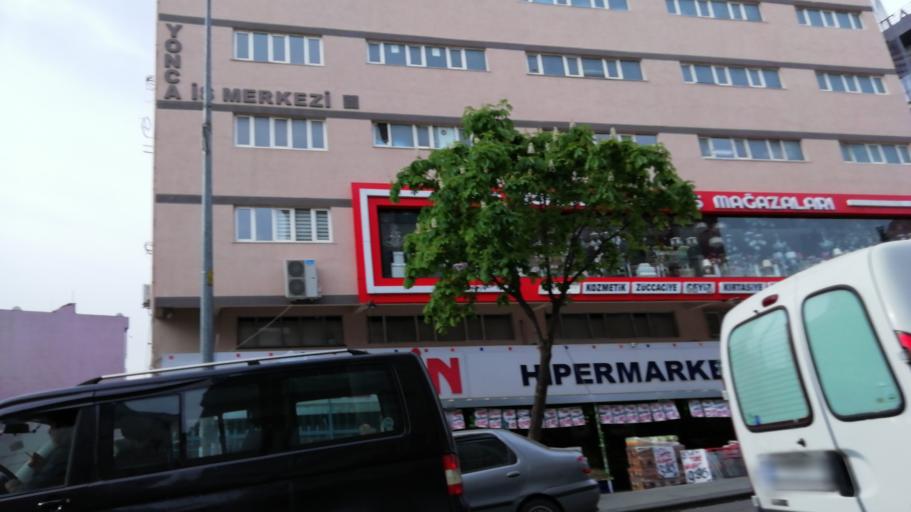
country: TR
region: Istanbul
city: Bagcilar
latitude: 41.0305
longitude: 28.8393
